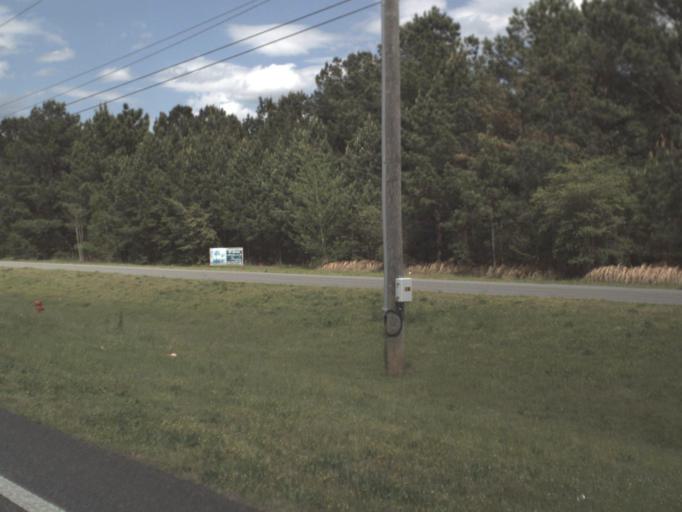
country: US
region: Florida
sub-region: Okaloosa County
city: Crestview
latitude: 30.7929
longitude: -86.5576
